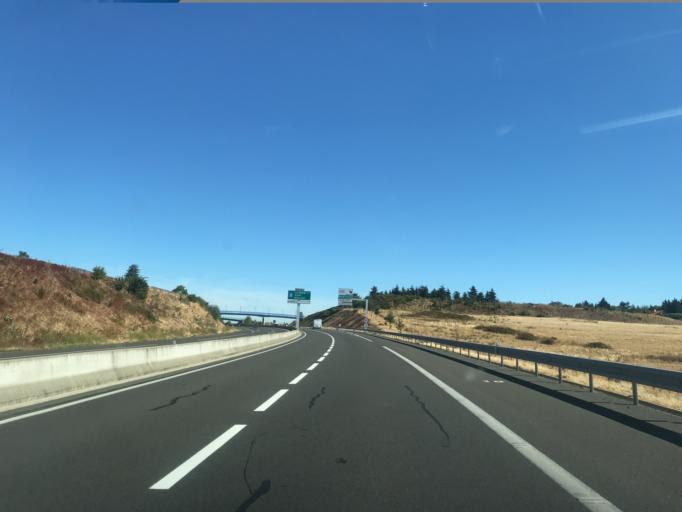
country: FR
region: Auvergne
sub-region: Departement de l'Allier
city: Premilhat
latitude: 46.3295
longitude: 2.5365
